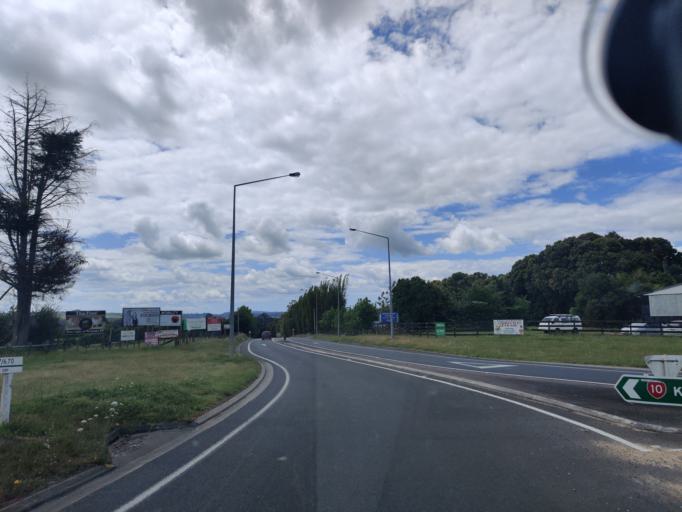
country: NZ
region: Northland
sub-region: Far North District
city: Kerikeri
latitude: -35.2537
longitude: 173.9318
